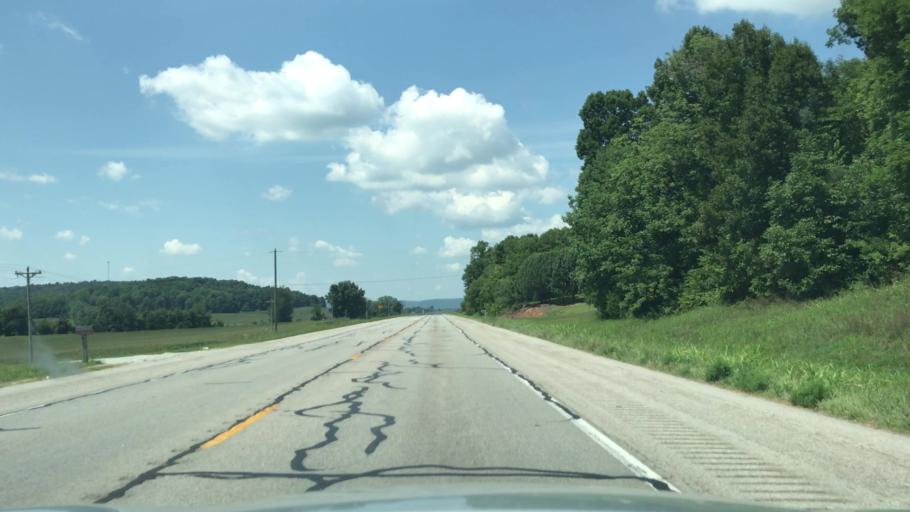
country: US
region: Kentucky
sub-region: Wayne County
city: Monticello
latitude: 36.7979
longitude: -84.9282
